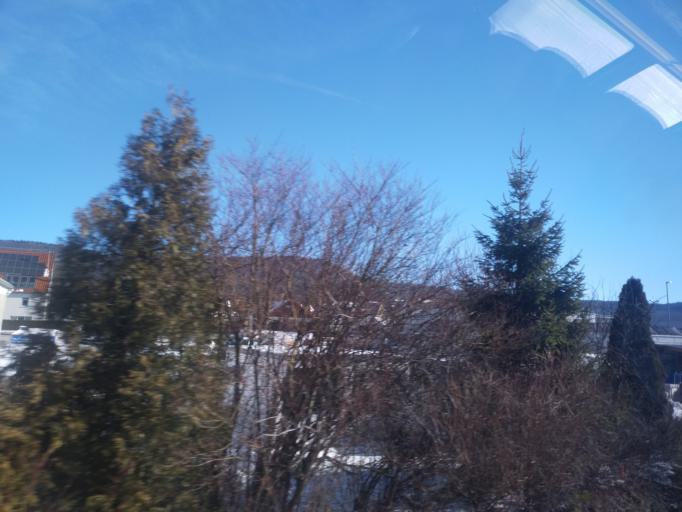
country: DE
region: Baden-Wuerttemberg
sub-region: Freiburg Region
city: Balgheim
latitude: 48.0643
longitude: 8.7631
